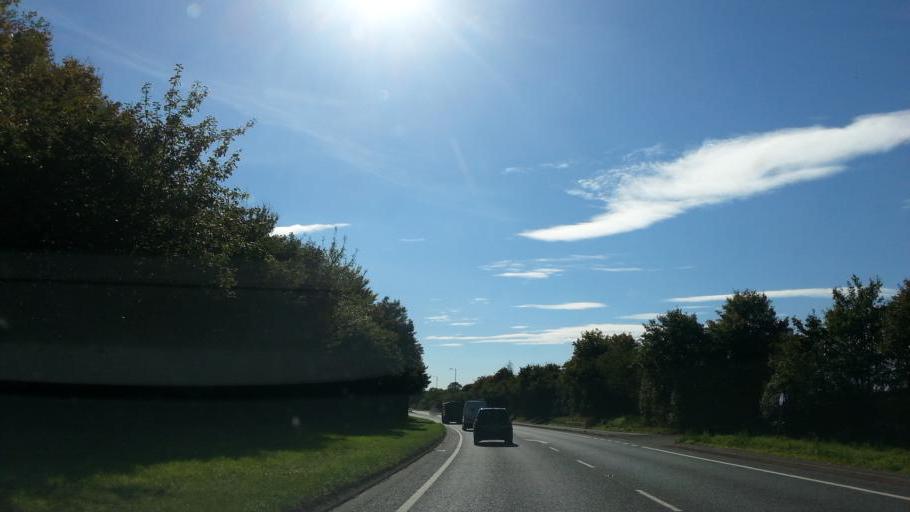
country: GB
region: England
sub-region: Telford and Wrekin
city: Chetwynd
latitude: 52.7488
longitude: -2.3960
